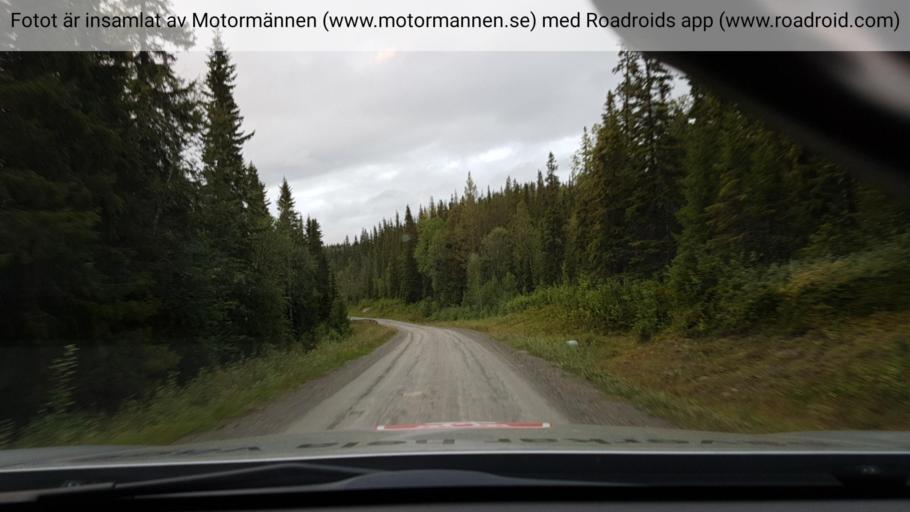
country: SE
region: Vaesterbotten
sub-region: Vilhelmina Kommun
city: Sjoberg
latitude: 65.5300
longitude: 15.4368
